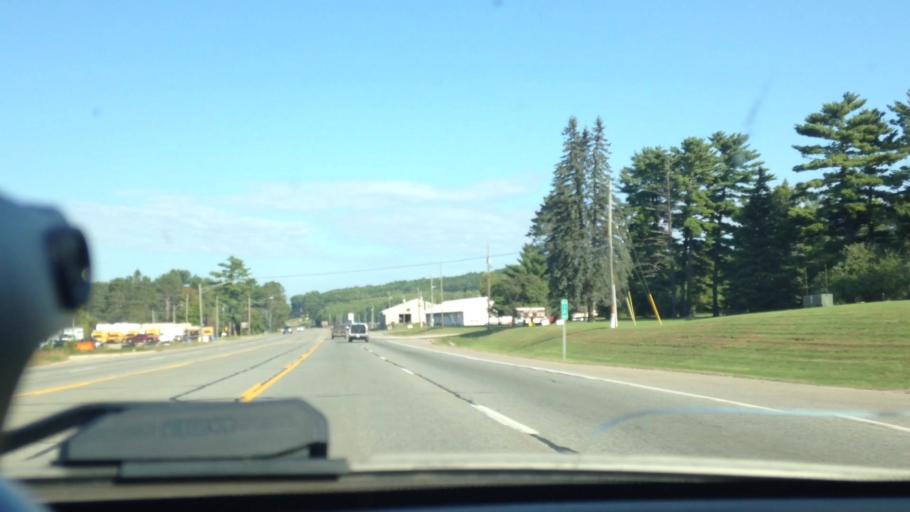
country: US
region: Michigan
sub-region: Dickinson County
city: Iron Mountain
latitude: 45.8472
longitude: -88.0504
